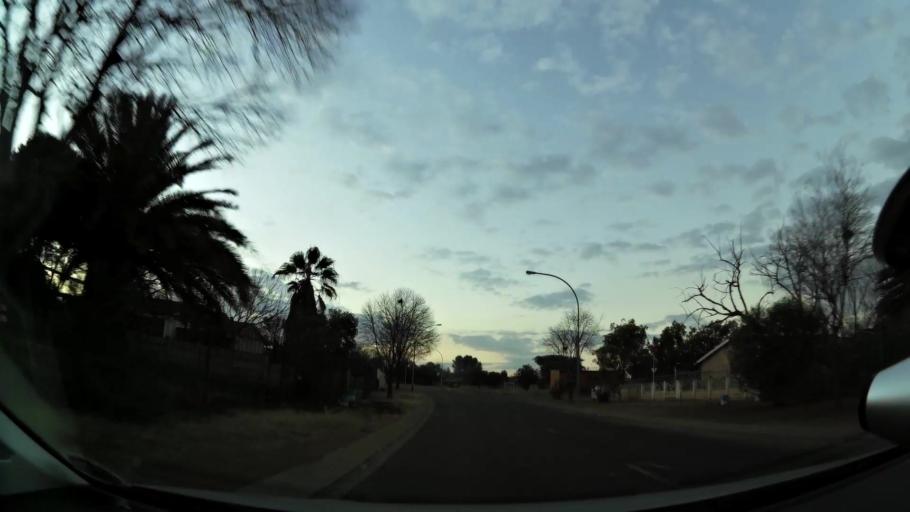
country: ZA
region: Orange Free State
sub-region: Mangaung Metropolitan Municipality
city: Bloemfontein
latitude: -29.1699
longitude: 26.1932
